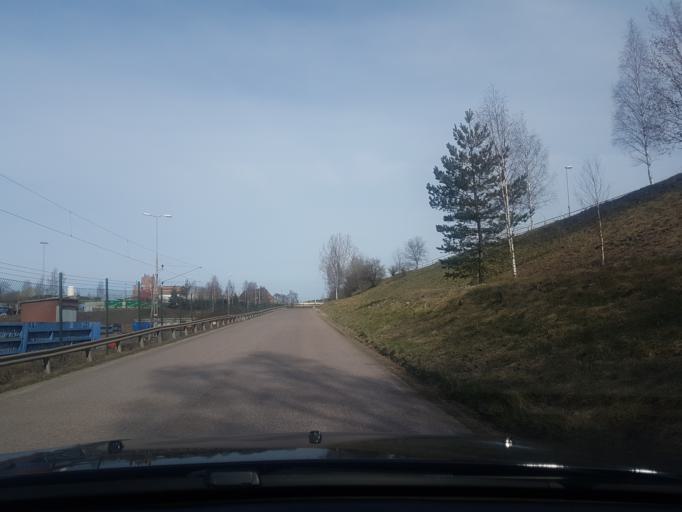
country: SE
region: Dalarna
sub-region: Borlange Kommun
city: Borlaenge
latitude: 60.4947
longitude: 15.4623
